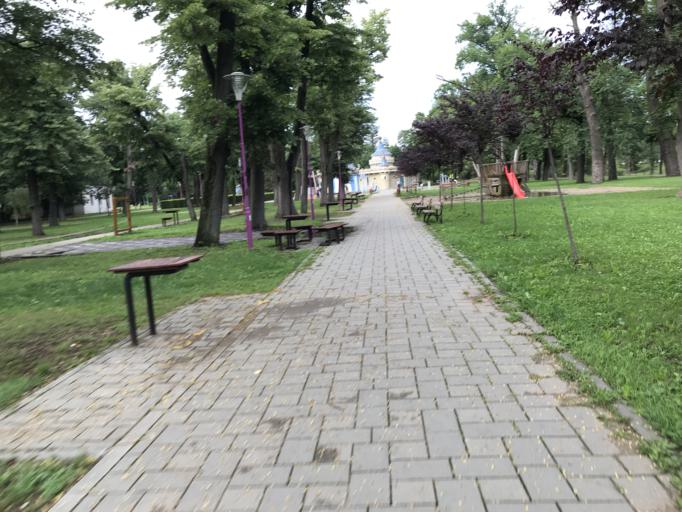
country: RO
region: Timis
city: Timisoara
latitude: 45.7529
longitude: 21.2376
